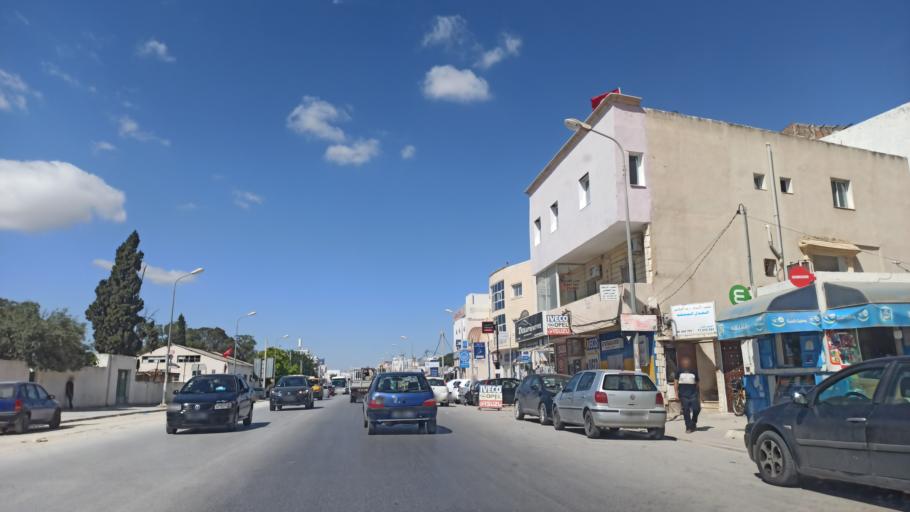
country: TN
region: Manouba
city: Manouba
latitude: 36.8002
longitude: 10.1080
